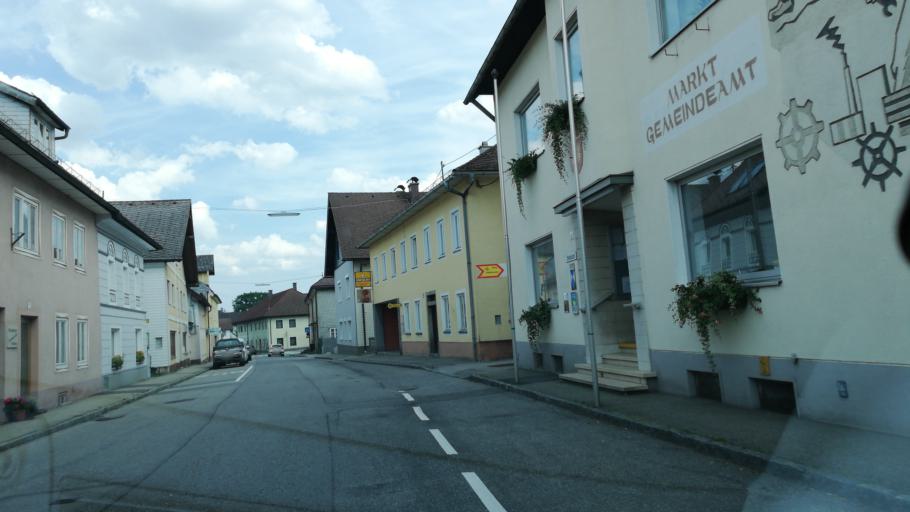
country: AT
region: Upper Austria
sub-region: Politischer Bezirk Vocklabruck
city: Attnang-Puchheim
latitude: 47.9911
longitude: 13.6885
